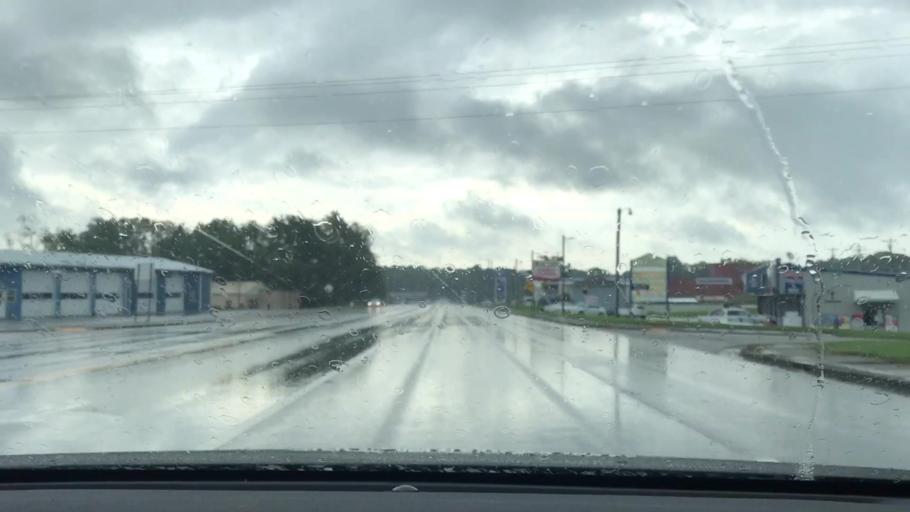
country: US
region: Tennessee
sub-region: Macon County
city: Lafayette
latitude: 36.5177
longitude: -86.0216
